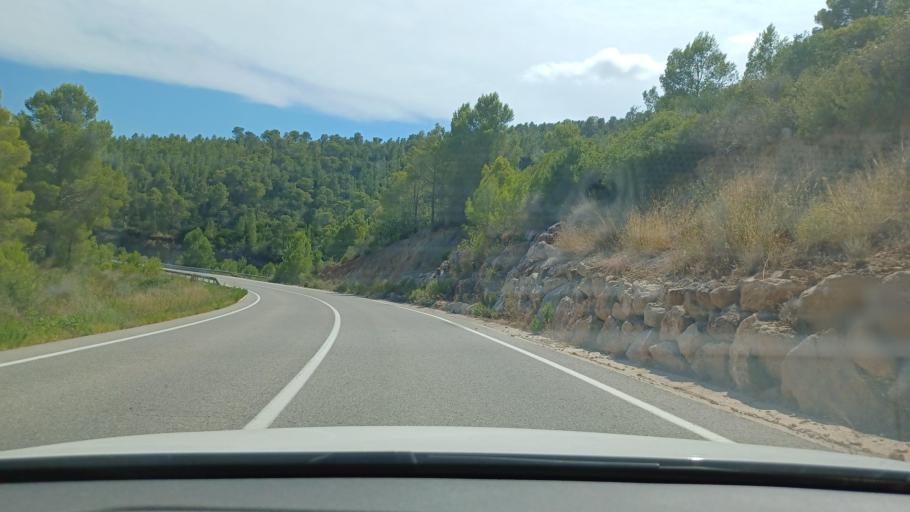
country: ES
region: Catalonia
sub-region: Provincia de Tarragona
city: Tivenys
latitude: 40.9429
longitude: 0.4587
